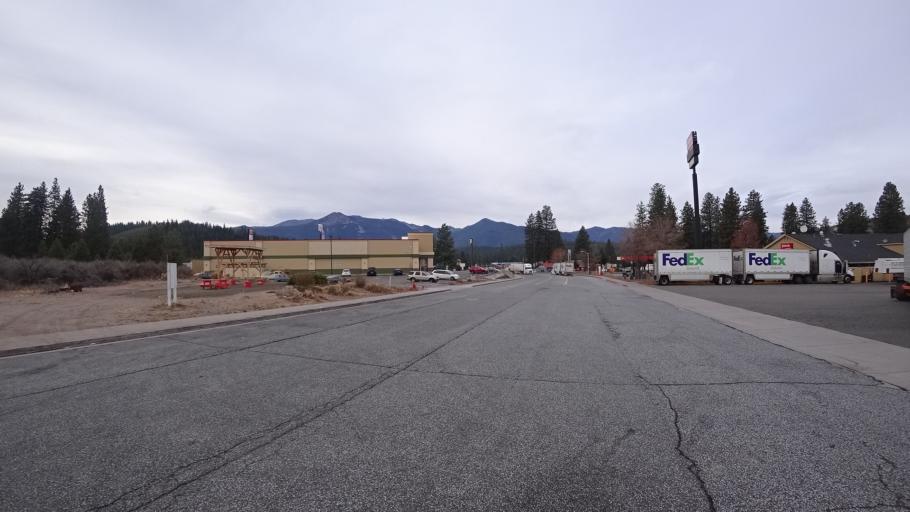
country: US
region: California
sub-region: Siskiyou County
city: Weed
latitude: 41.3987
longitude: -122.3757
